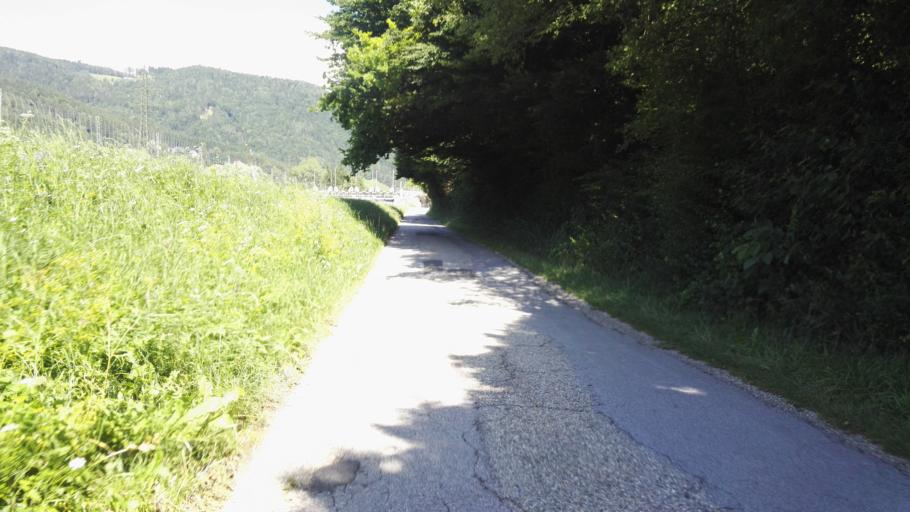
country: AT
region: Styria
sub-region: Politischer Bezirk Graz-Umgebung
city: Frohnleiten
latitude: 47.2311
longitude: 15.3226
